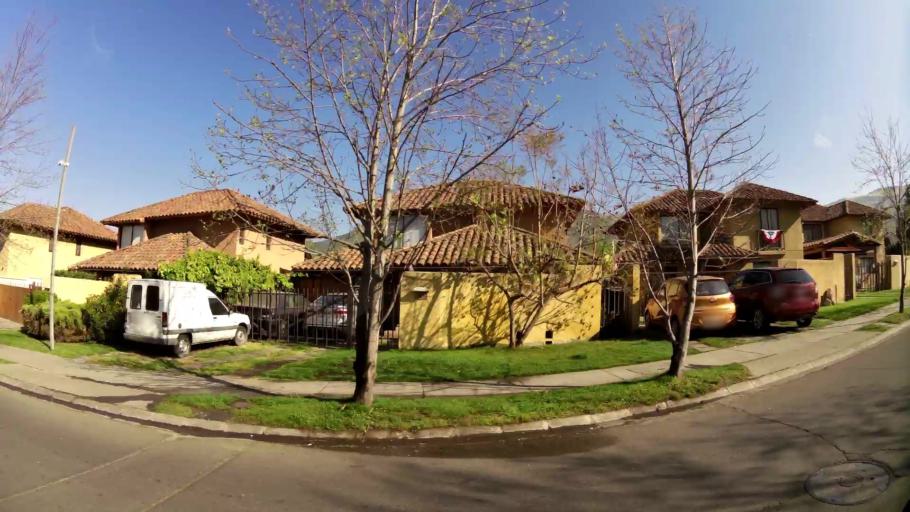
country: CL
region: Santiago Metropolitan
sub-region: Provincia de Chacabuco
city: Chicureo Abajo
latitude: -33.3458
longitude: -70.6683
